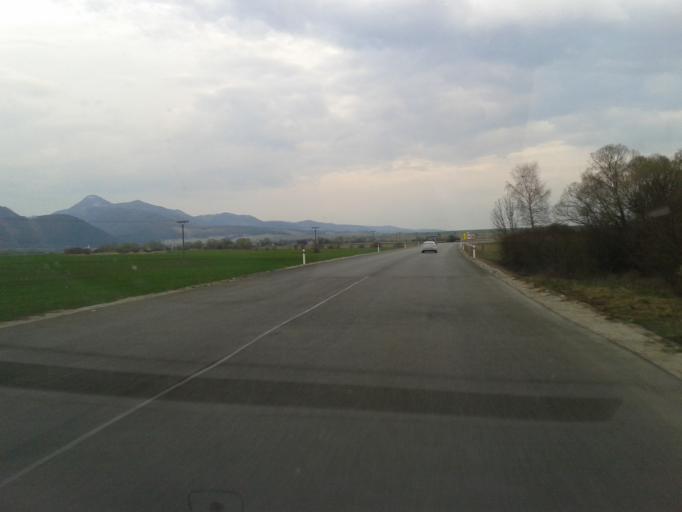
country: SK
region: Zilinsky
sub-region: Okres Martin
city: Martin
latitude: 48.9677
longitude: 18.9068
